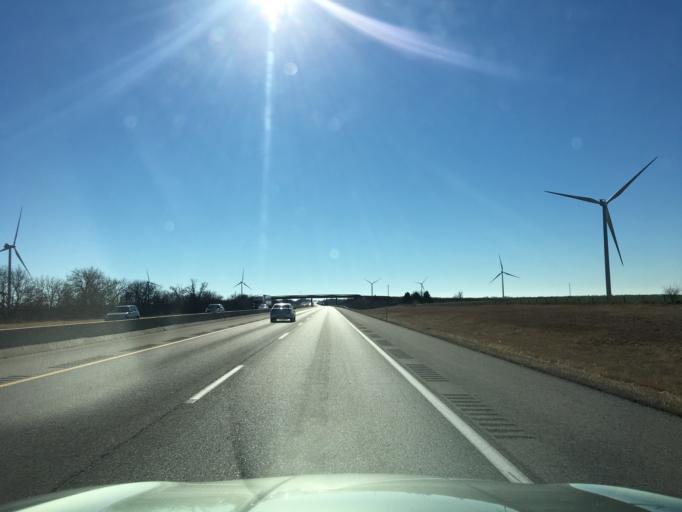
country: US
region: Kansas
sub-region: Sumner County
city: Wellington
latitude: 37.1482
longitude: -97.3395
